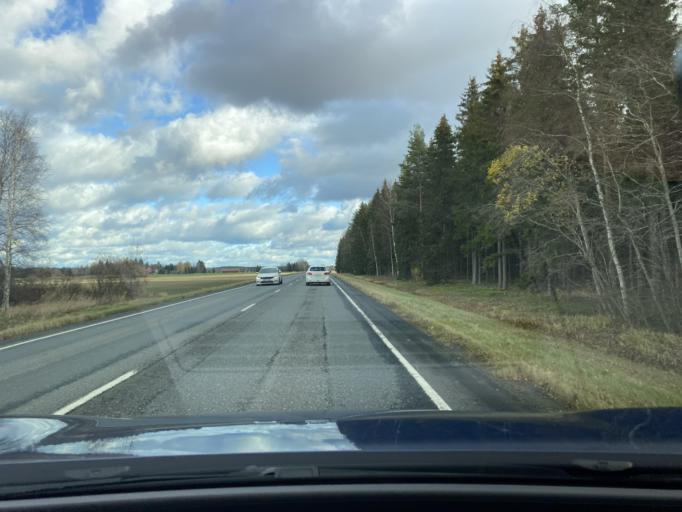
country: FI
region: Haeme
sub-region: Forssa
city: Humppila
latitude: 60.9462
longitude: 23.3085
